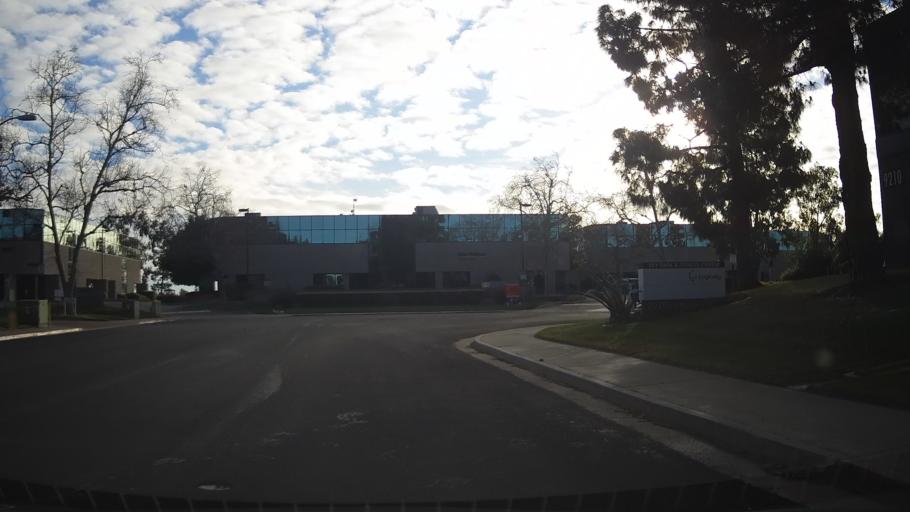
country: US
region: California
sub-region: San Diego County
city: San Diego
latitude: 32.8149
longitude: -117.1275
